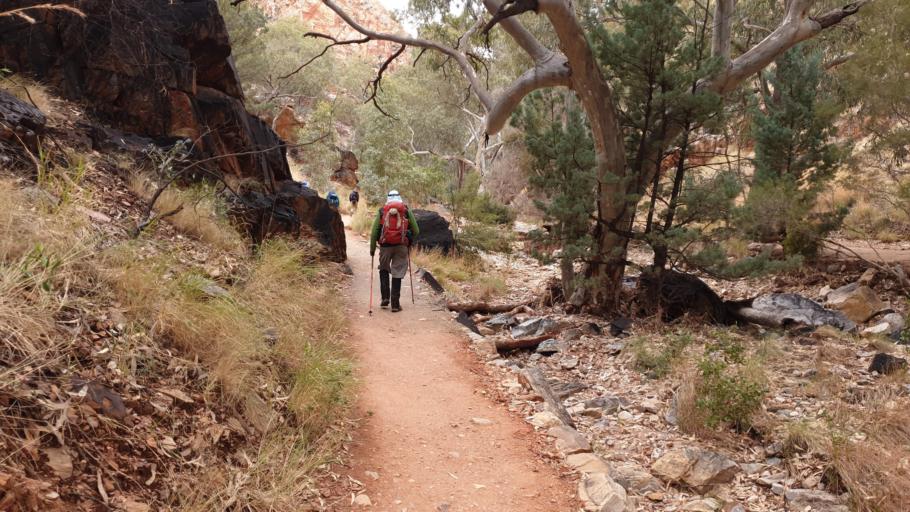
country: AU
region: Northern Territory
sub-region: Alice Springs
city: Alice Springs
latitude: -23.7211
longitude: 133.4695
